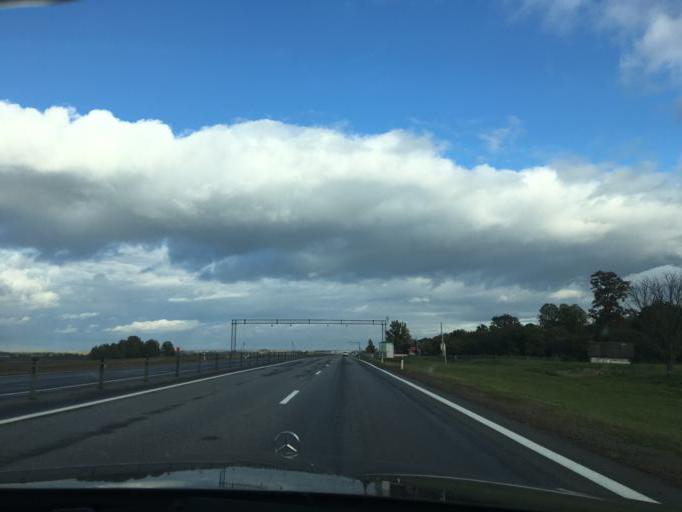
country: BY
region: Vitebsk
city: Orsha
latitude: 54.6344
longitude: 30.5251
